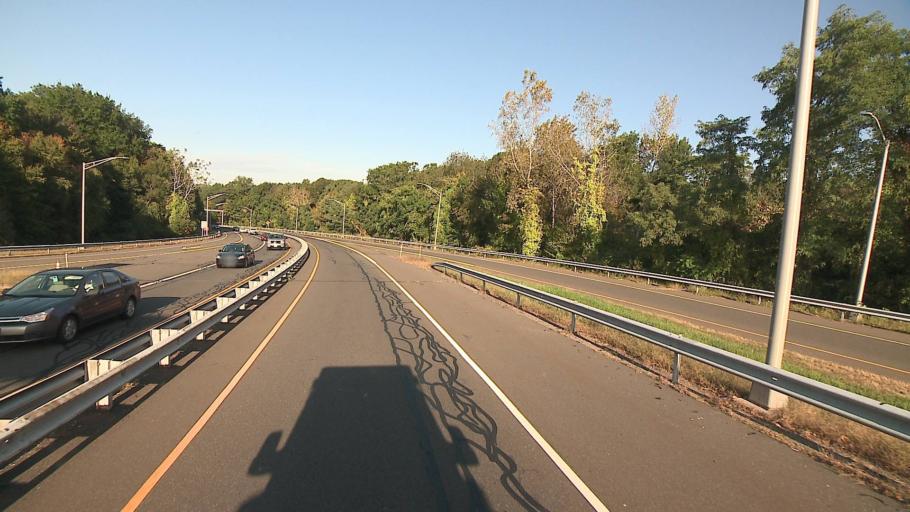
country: US
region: Connecticut
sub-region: New Haven County
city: City of Milford (balance)
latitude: 41.2519
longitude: -73.0790
